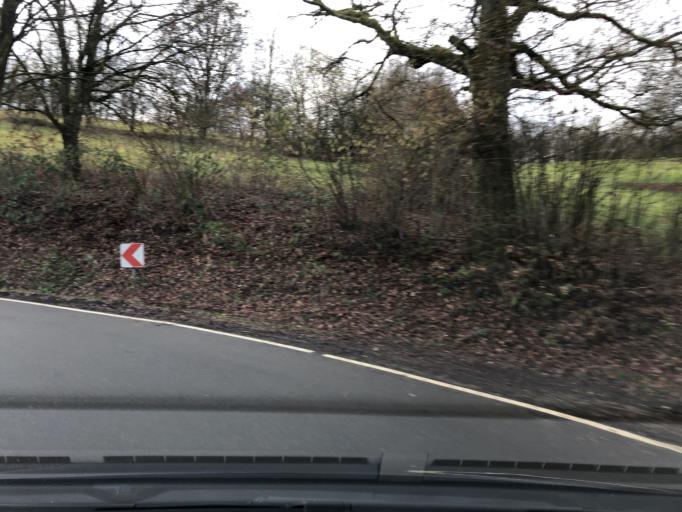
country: DE
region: Hesse
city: Neckarsteinach
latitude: 49.3859
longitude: 8.8565
